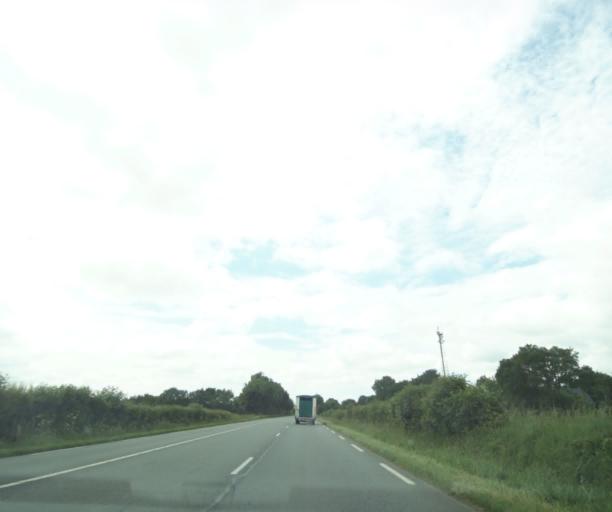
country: FR
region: Poitou-Charentes
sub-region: Departement des Deux-Sevres
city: Champdeniers-Saint-Denis
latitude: 46.4994
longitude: -0.3411
